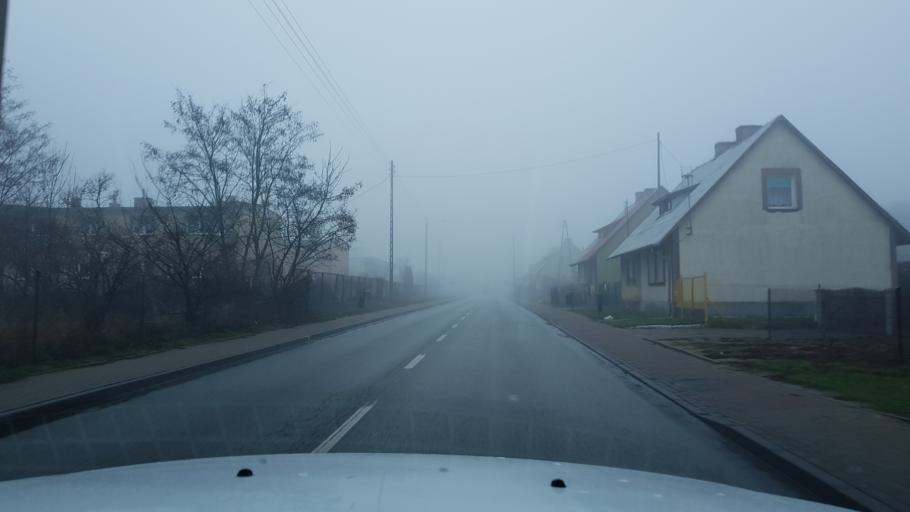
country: PL
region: West Pomeranian Voivodeship
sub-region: Powiat mysliborski
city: Mysliborz
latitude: 52.9489
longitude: 14.7907
